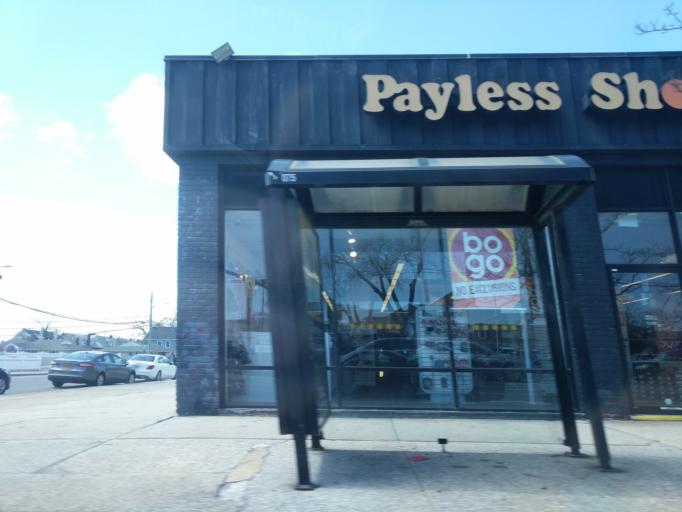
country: US
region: New York
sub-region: Nassau County
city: Oceanside
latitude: 40.6345
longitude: -73.6406
